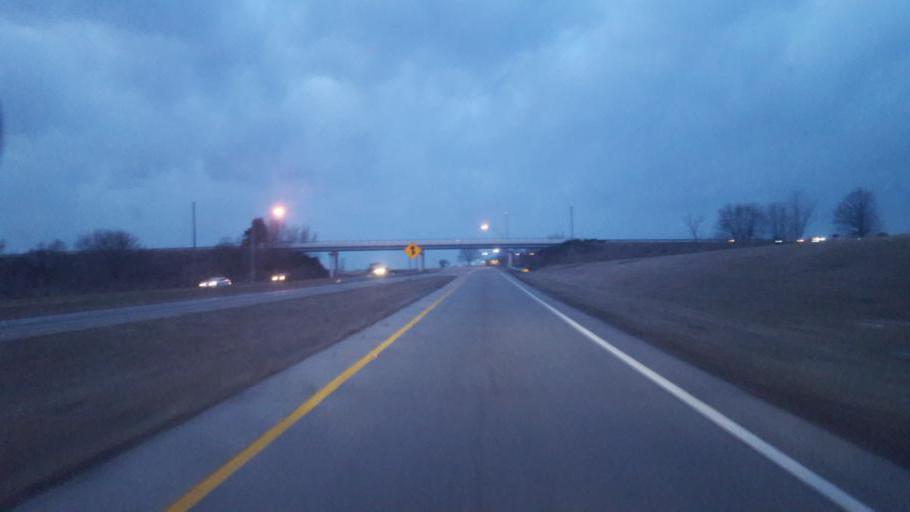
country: US
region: Ohio
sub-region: Ross County
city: Chillicothe
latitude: 39.3905
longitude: -82.9696
